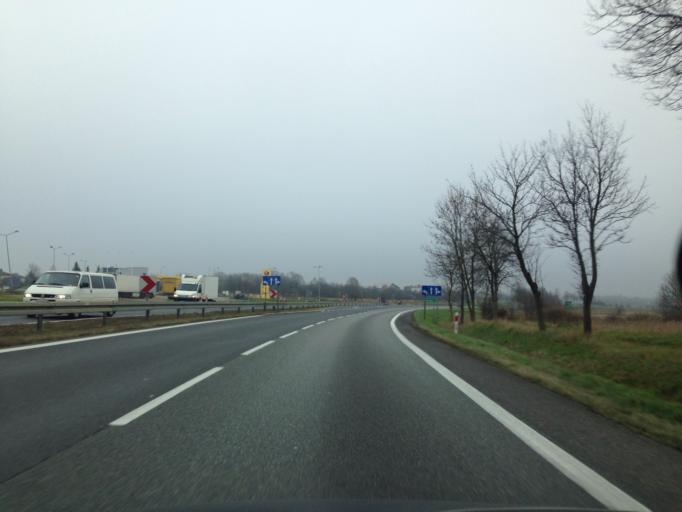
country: PL
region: Silesian Voivodeship
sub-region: Powiat myszkowski
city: Kozieglowy
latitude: 50.6077
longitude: 19.1546
